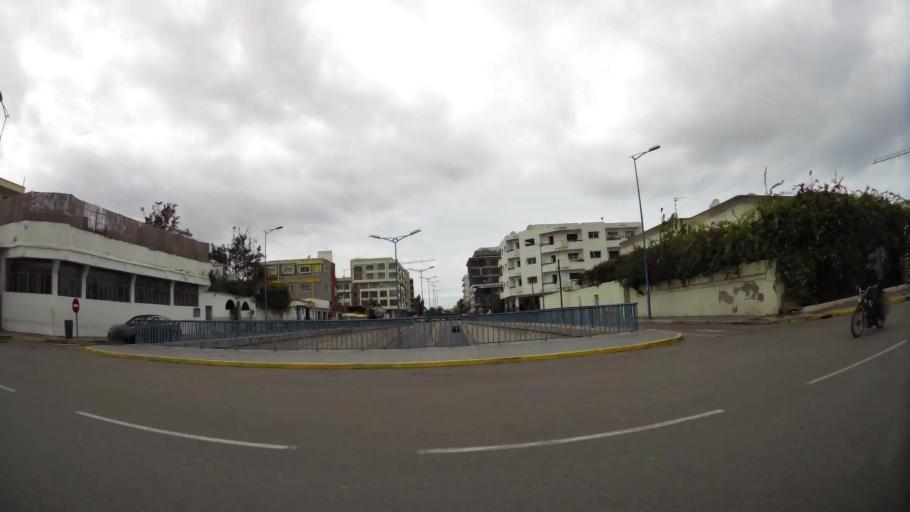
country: MA
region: Grand Casablanca
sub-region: Casablanca
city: Casablanca
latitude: 33.5558
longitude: -7.6312
